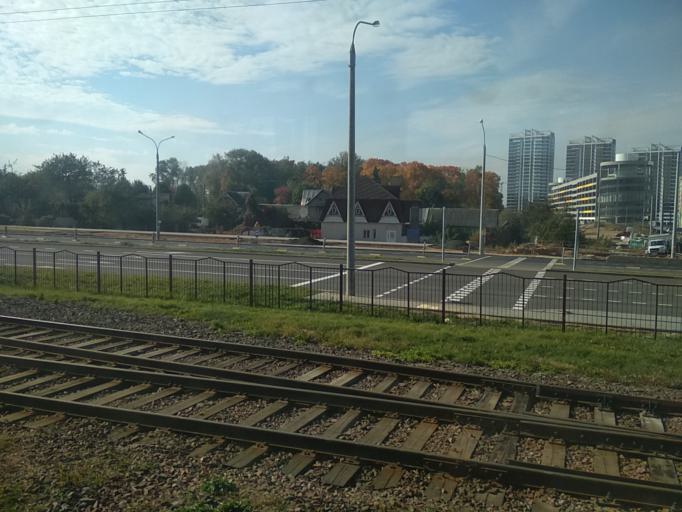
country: BY
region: Minsk
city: Minsk
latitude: 53.8691
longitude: 27.5612
